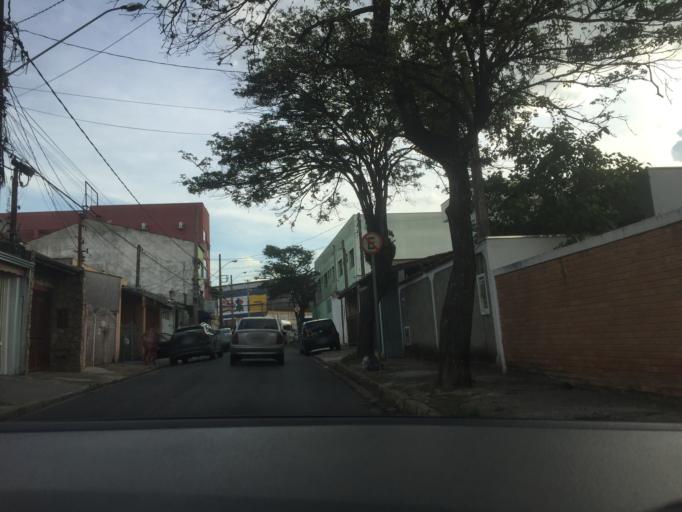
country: BR
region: Sao Paulo
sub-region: Varzea Paulista
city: Varzea Paulista
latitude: -23.2080
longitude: -46.8484
